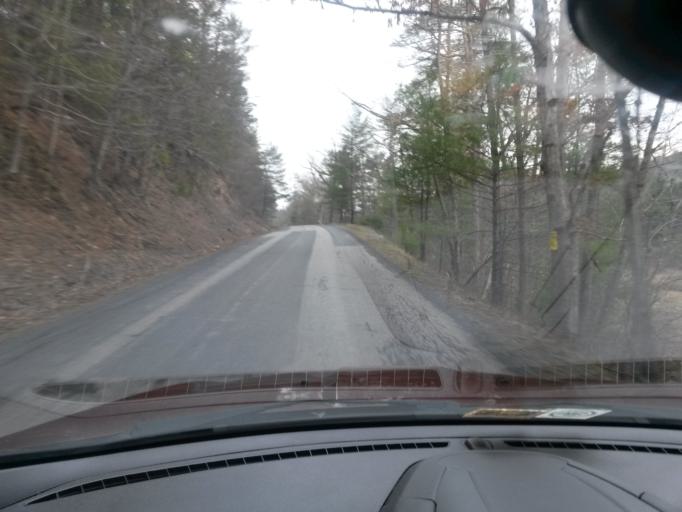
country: US
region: Virginia
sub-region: Bath County
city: Warm Springs
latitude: 38.0344
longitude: -79.8575
